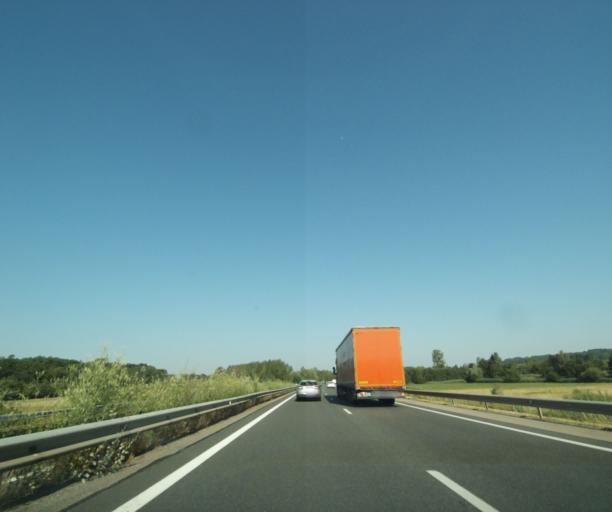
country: FR
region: Lorraine
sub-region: Departement de Meurthe-et-Moselle
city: Damelevieres
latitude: 48.5928
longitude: 6.4038
